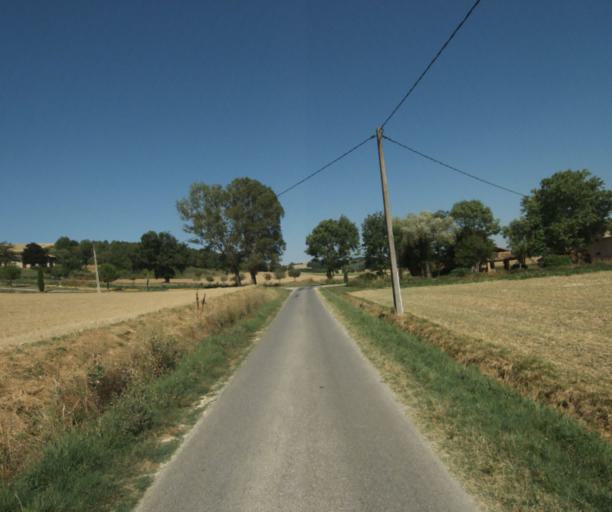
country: FR
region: Midi-Pyrenees
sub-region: Departement du Tarn
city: Puylaurens
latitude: 43.5196
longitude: 1.9440
